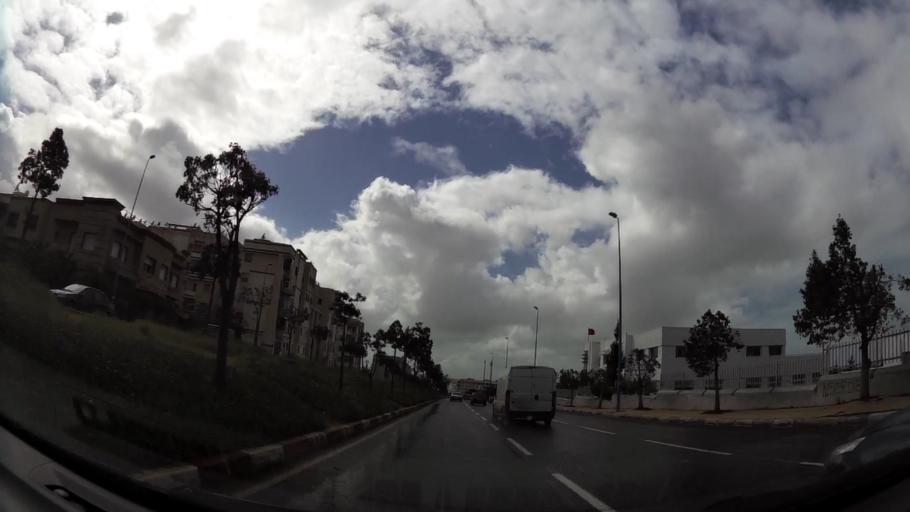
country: MA
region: Grand Casablanca
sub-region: Casablanca
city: Casablanca
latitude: 33.5308
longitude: -7.6442
